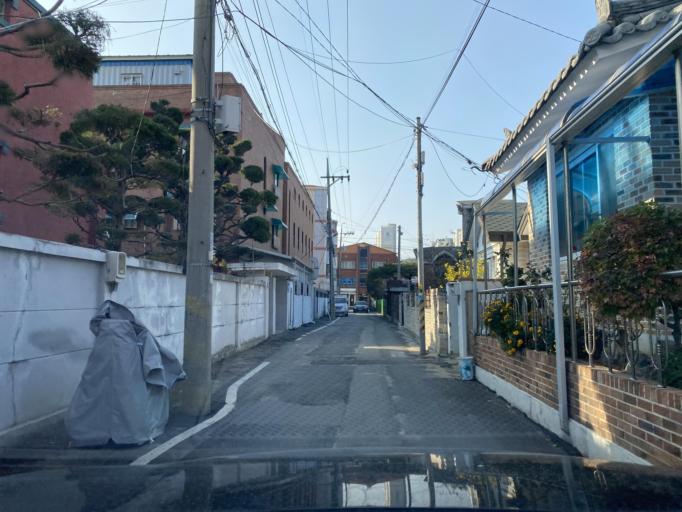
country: KR
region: Chungcheongnam-do
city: Yesan
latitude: 36.6813
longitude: 126.8506
